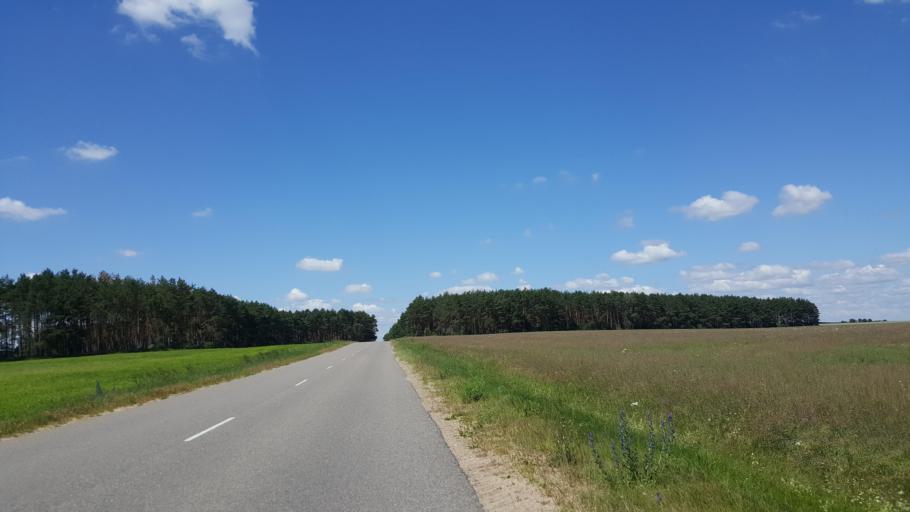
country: BY
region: Brest
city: Kamyanyets
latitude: 52.3901
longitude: 23.7464
